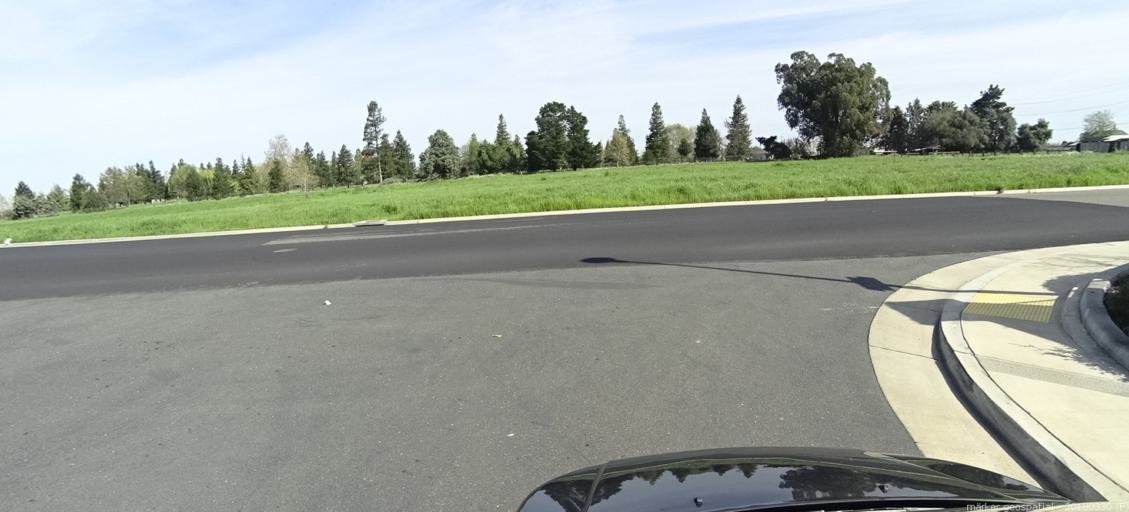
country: US
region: California
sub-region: Sacramento County
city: Vineyard
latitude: 38.4888
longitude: -121.3367
